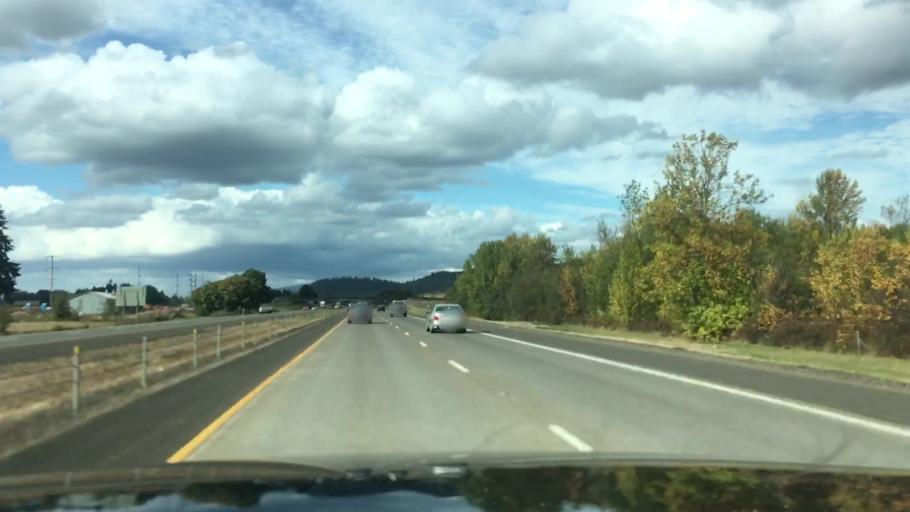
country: US
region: Oregon
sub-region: Lane County
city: Creswell
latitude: 43.9327
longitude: -123.0097
